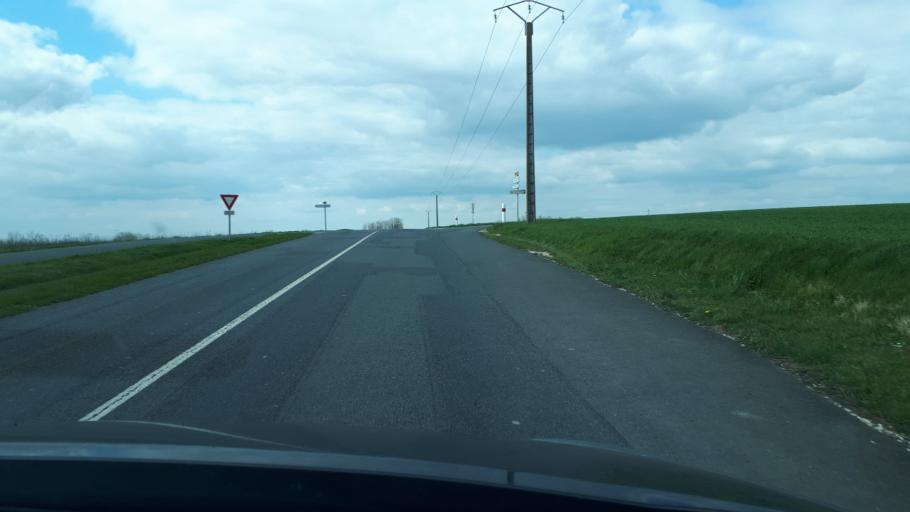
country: FR
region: Centre
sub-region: Departement du Loir-et-Cher
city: Lunay
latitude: 47.7666
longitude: 0.9247
